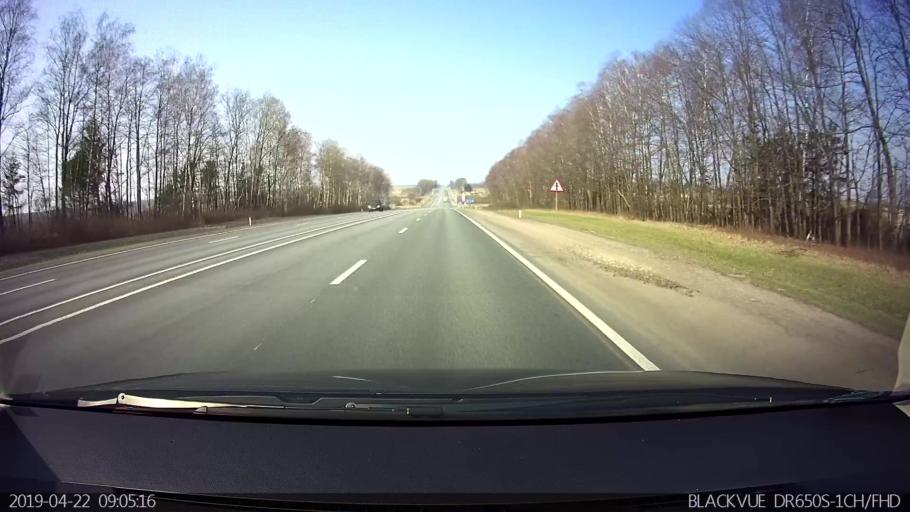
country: RU
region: Smolensk
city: Katyn'
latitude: 54.8496
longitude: 31.8116
